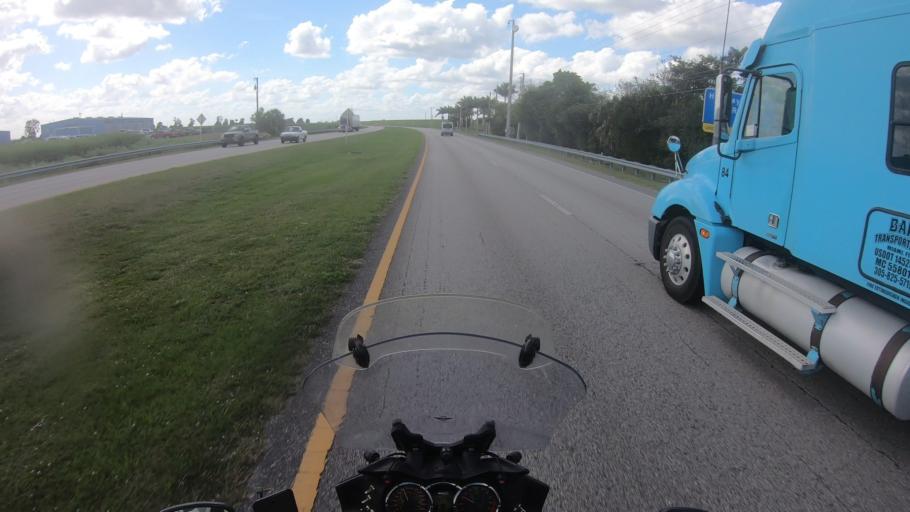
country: US
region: Florida
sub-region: Palm Beach County
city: South Bay
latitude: 26.6797
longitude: -80.7292
